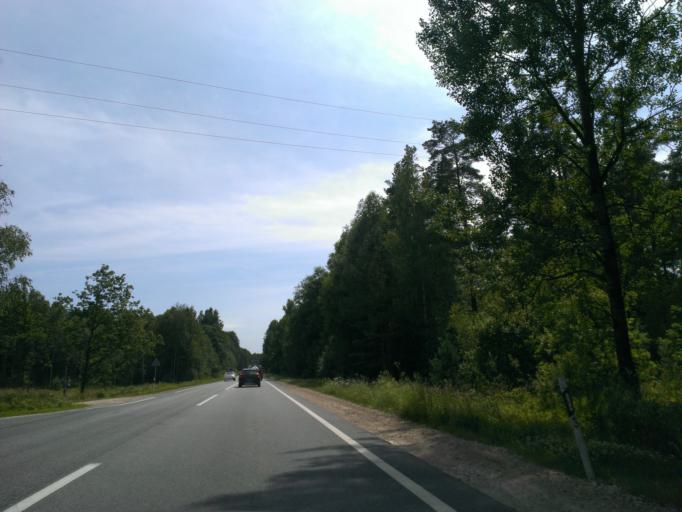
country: LV
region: Salaspils
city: Salaspils
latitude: 56.9178
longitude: 24.3980
